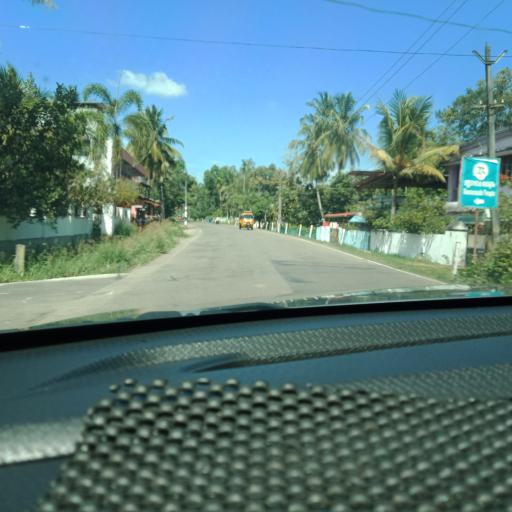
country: IN
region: Kerala
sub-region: Alappuzha
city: Mavelikara
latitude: 9.2888
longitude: 76.4560
